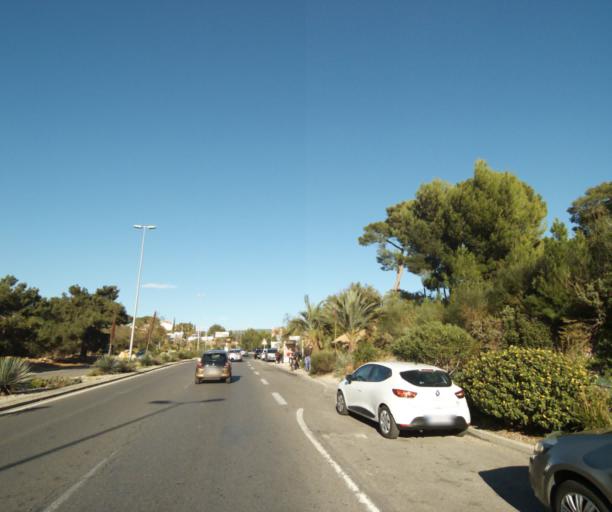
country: FR
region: Provence-Alpes-Cote d'Azur
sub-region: Departement des Bouches-du-Rhone
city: La Ciotat
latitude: 43.1903
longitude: 5.6042
